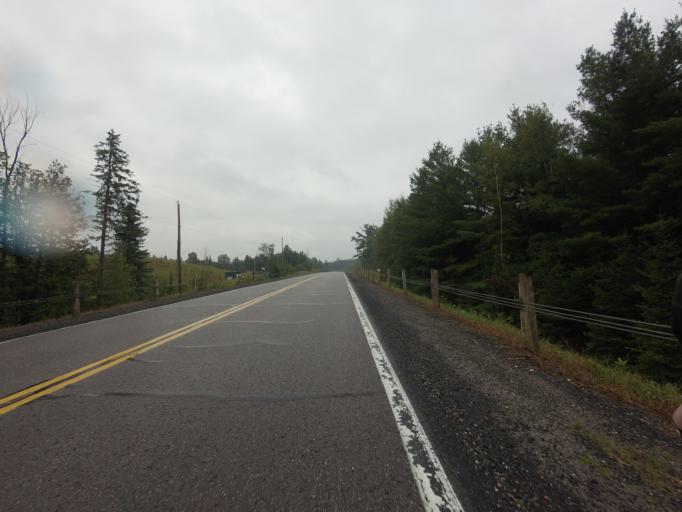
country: CA
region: Ontario
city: Perth
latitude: 45.0874
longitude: -76.4224
